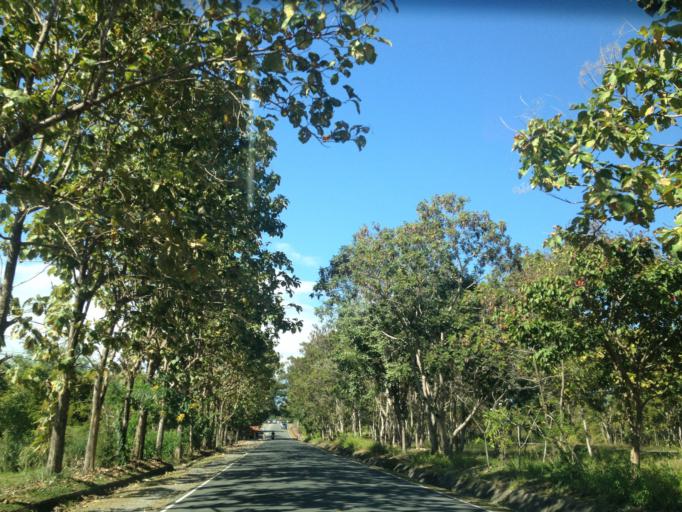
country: TH
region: Chiang Mai
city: Chiang Mai
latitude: 18.8617
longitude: 98.9487
